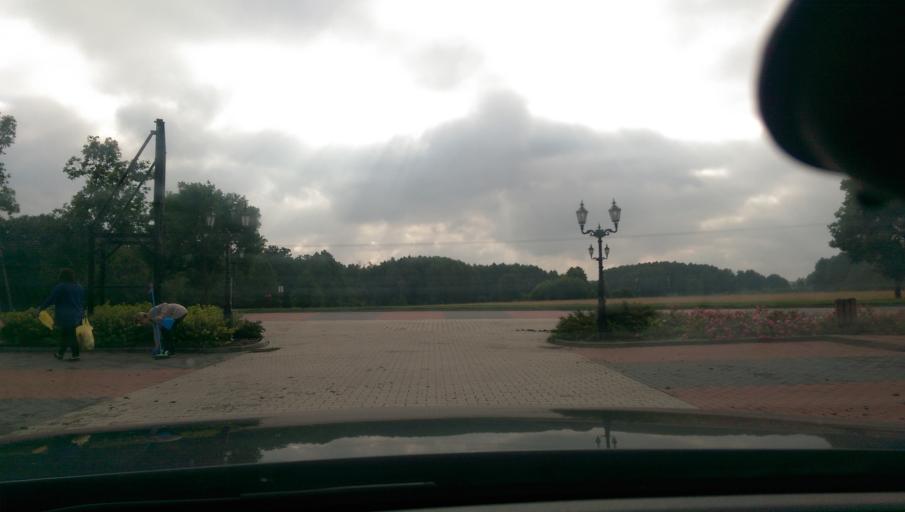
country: PL
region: Masovian Voivodeship
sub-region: Powiat przasnyski
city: Przasnysz
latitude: 53.1001
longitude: 20.8535
